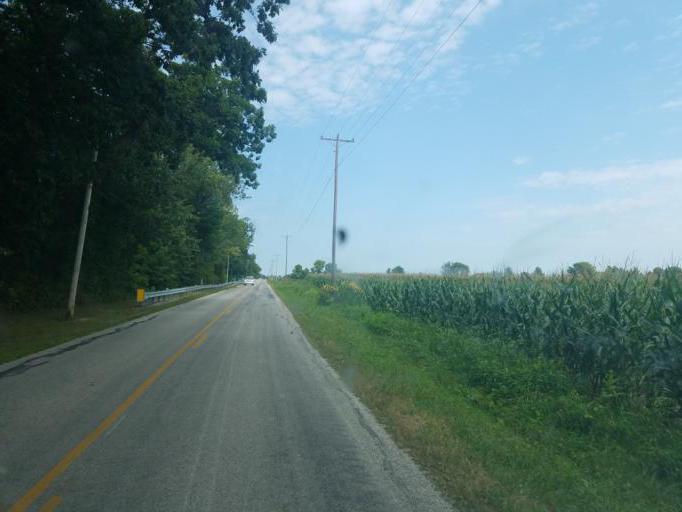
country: US
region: Ohio
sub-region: Marion County
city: Marion
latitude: 40.5506
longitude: -83.2181
